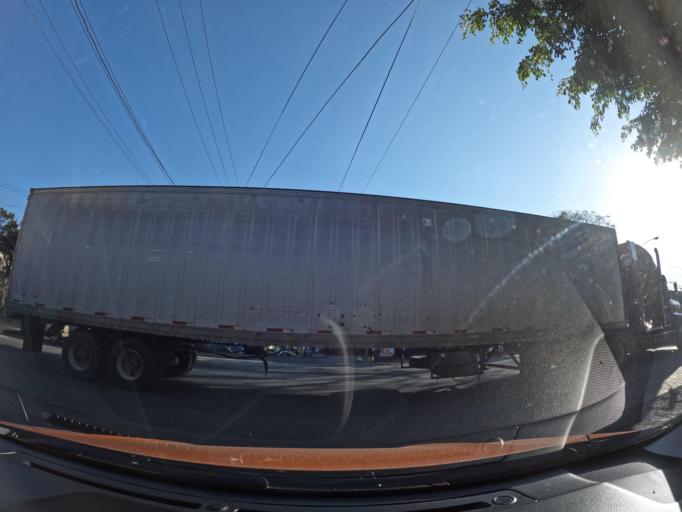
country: GT
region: Escuintla
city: Palin
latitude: 14.4036
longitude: -90.6973
